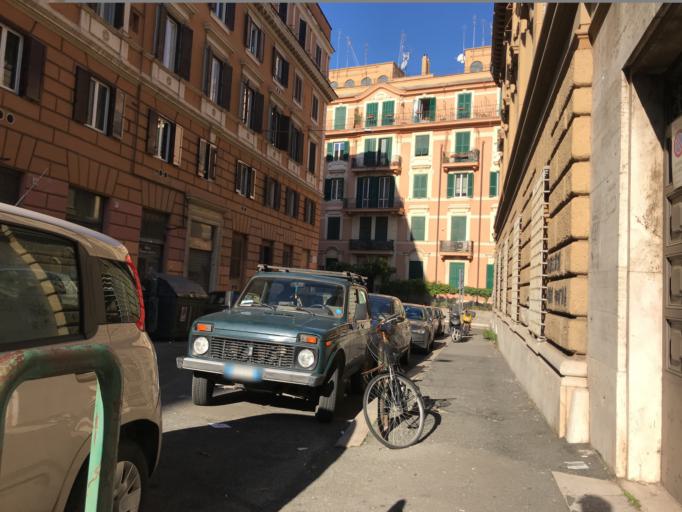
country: IT
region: Latium
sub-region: Citta metropolitana di Roma Capitale
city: Rome
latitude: 41.9128
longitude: 12.5022
